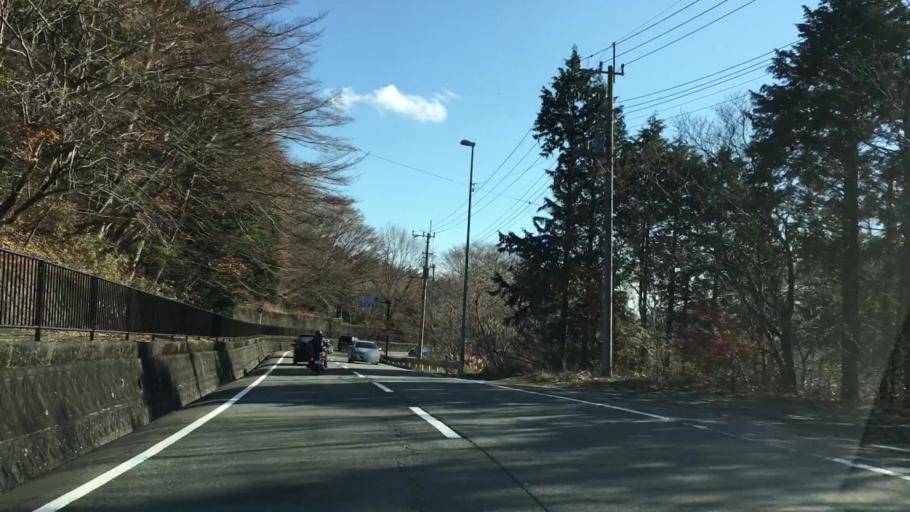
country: JP
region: Shizuoka
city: Gotemba
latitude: 35.3665
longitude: 138.8587
